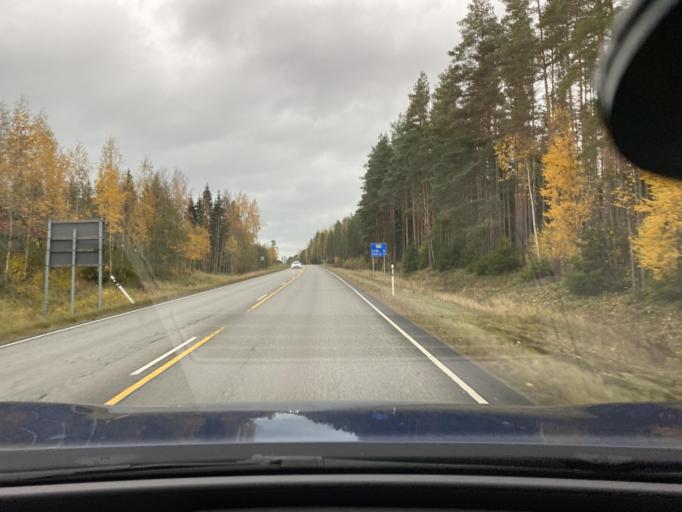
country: FI
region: Varsinais-Suomi
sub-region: Loimaa
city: Ylaene
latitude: 60.8890
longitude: 22.4033
